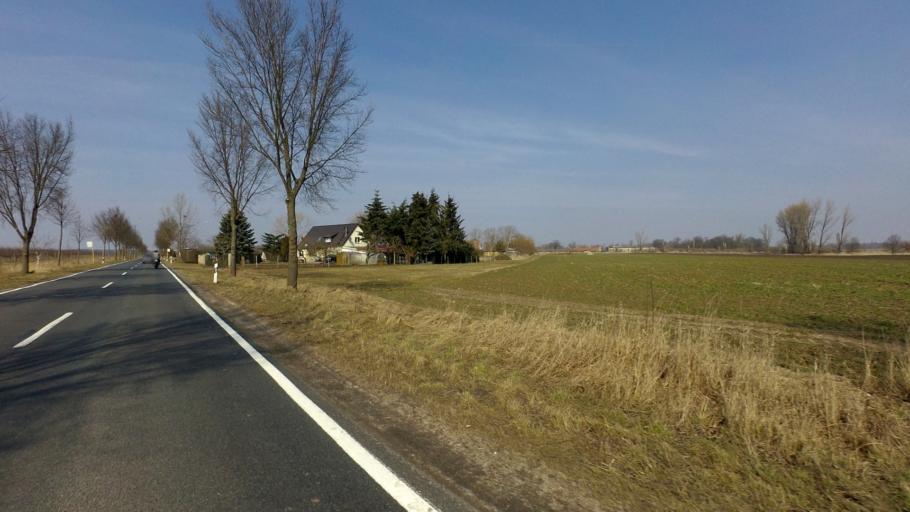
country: DE
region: Brandenburg
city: Ketzin
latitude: 52.4486
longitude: 12.8381
